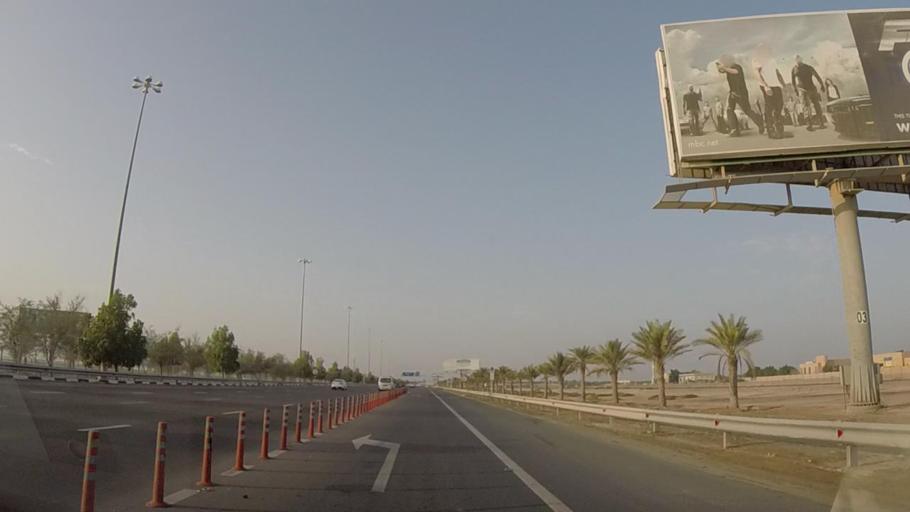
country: AE
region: Dubai
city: Dubai
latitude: 24.8695
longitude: 54.9158
